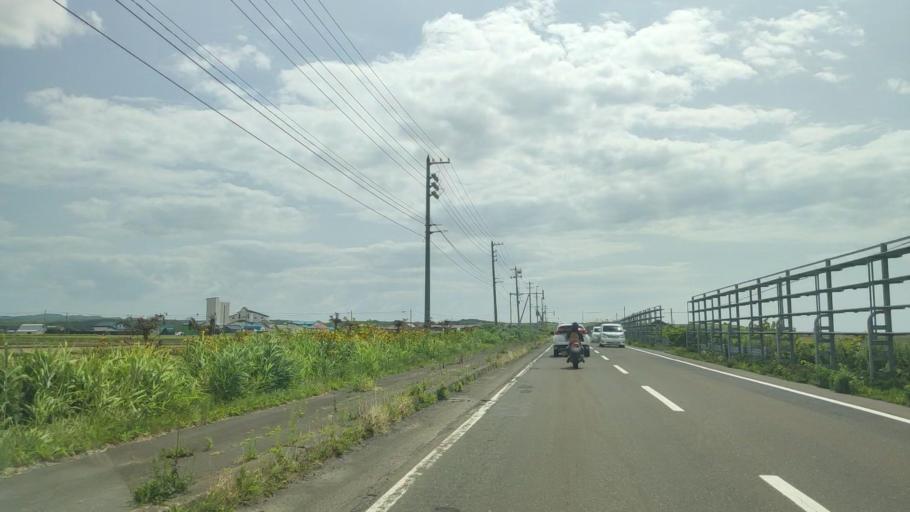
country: JP
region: Hokkaido
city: Rumoi
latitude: 44.4545
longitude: 141.7592
